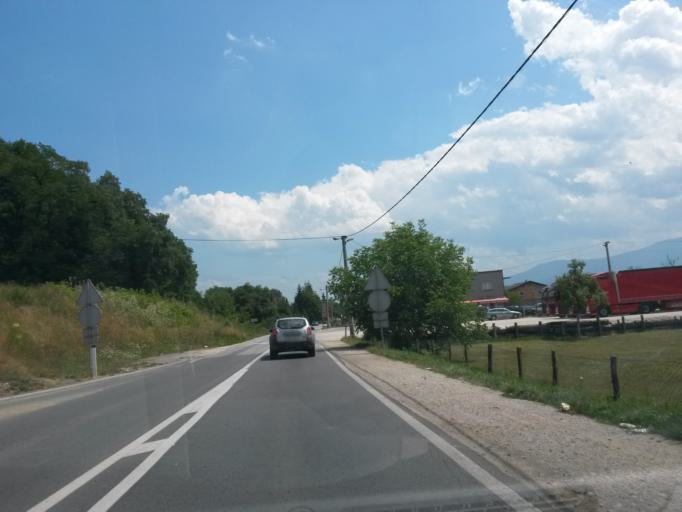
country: BA
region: Federation of Bosnia and Herzegovina
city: Vitez
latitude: 44.1894
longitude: 17.7389
